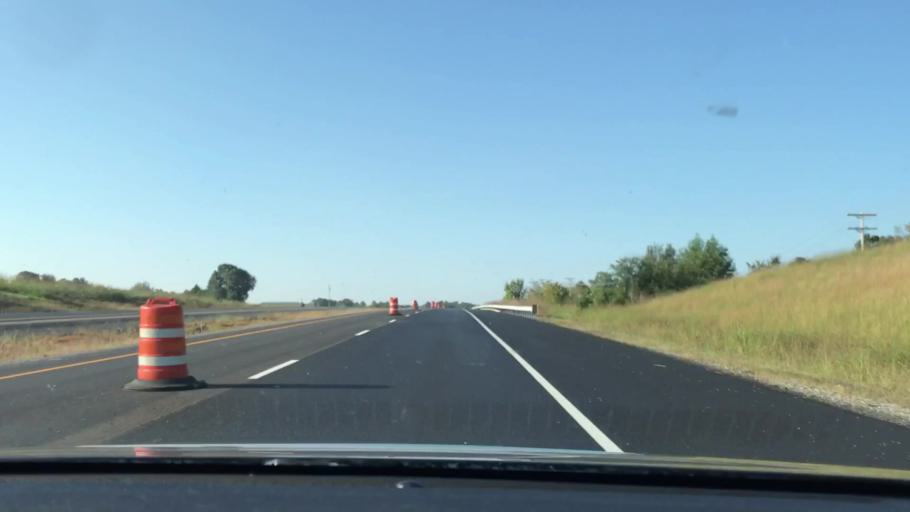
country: US
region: Kentucky
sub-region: Trigg County
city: Cadiz
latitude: 36.8486
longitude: -87.8207
